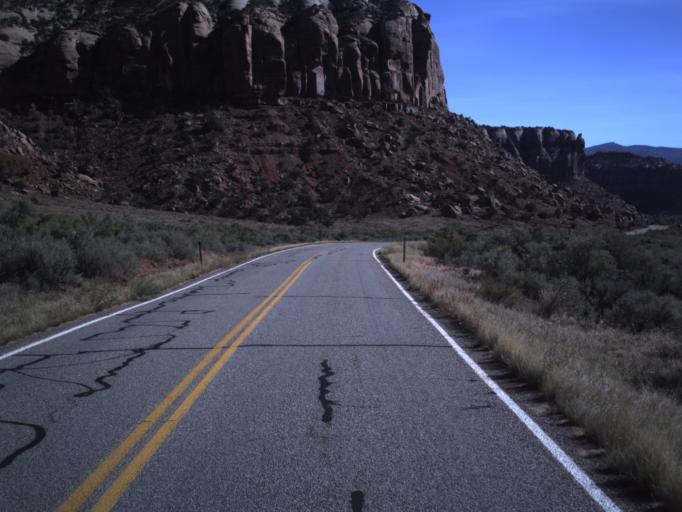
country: US
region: Utah
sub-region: San Juan County
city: Monticello
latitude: 38.0529
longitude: -109.5530
